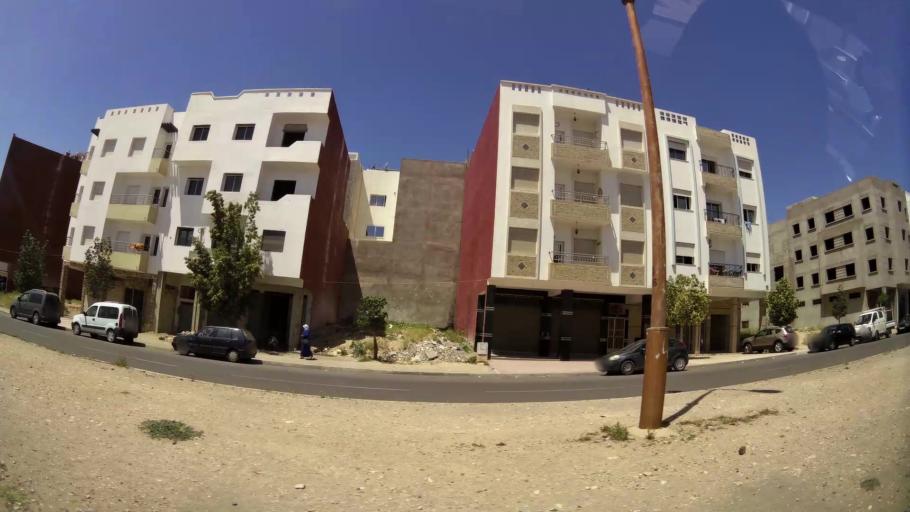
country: MA
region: Oued ed Dahab-Lagouira
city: Dakhla
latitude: 30.4295
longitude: -9.5568
